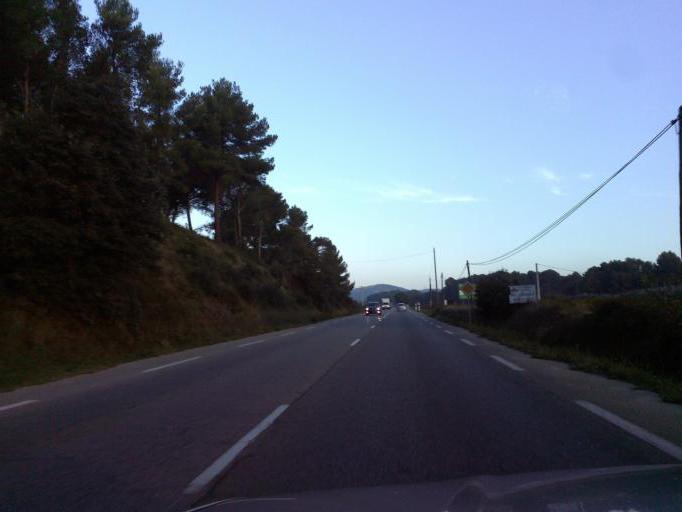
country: FR
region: Provence-Alpes-Cote d'Azur
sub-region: Departement des Bouches-du-Rhone
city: Lambesc
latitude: 43.6639
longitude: 5.2513
